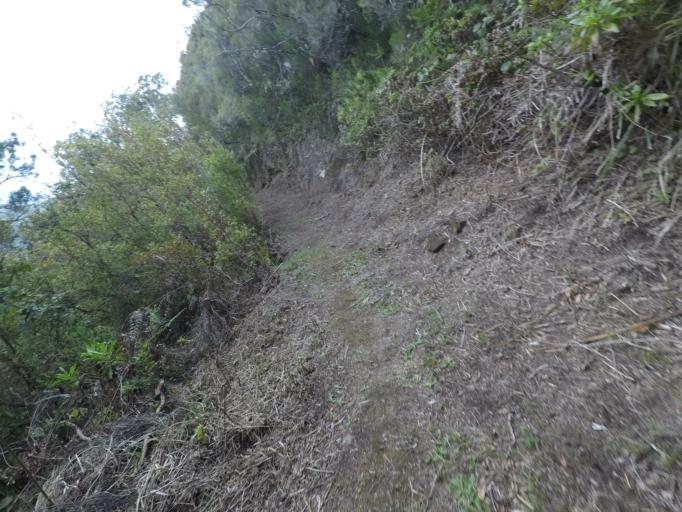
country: PT
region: Madeira
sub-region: Camara de Lobos
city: Curral das Freiras
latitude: 32.7654
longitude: -16.9757
